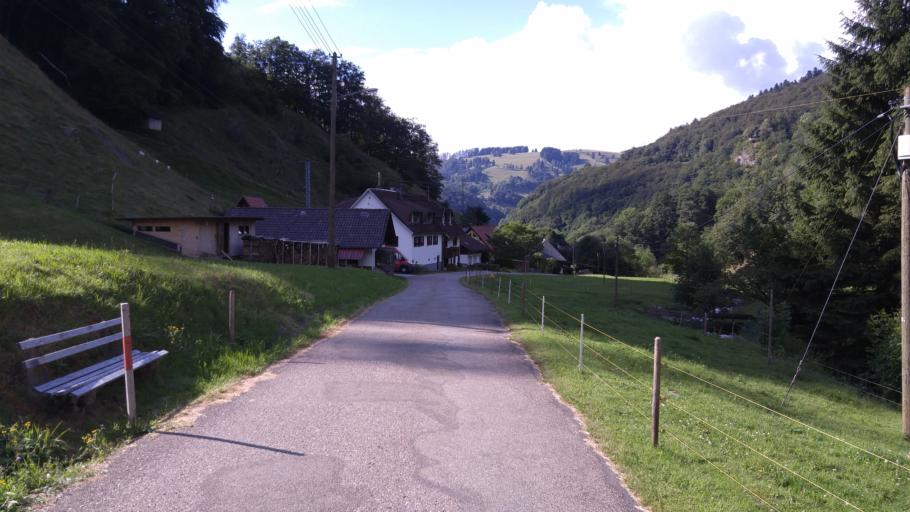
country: DE
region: Baden-Wuerttemberg
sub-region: Freiburg Region
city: Wieden
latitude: 47.8674
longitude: 7.8475
